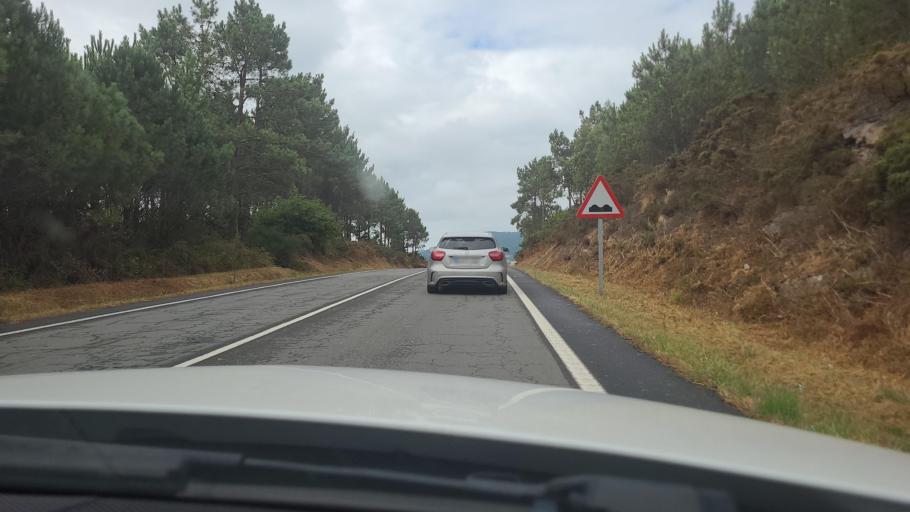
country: ES
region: Galicia
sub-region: Provincia da Coruna
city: Fisterra
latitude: 42.9300
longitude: -9.2367
